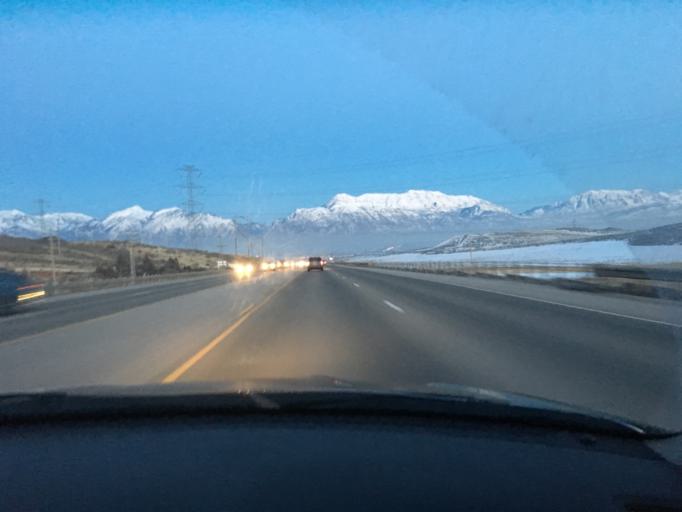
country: US
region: Utah
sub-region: Utah County
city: Saratoga Springs
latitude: 40.3834
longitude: -111.9577
